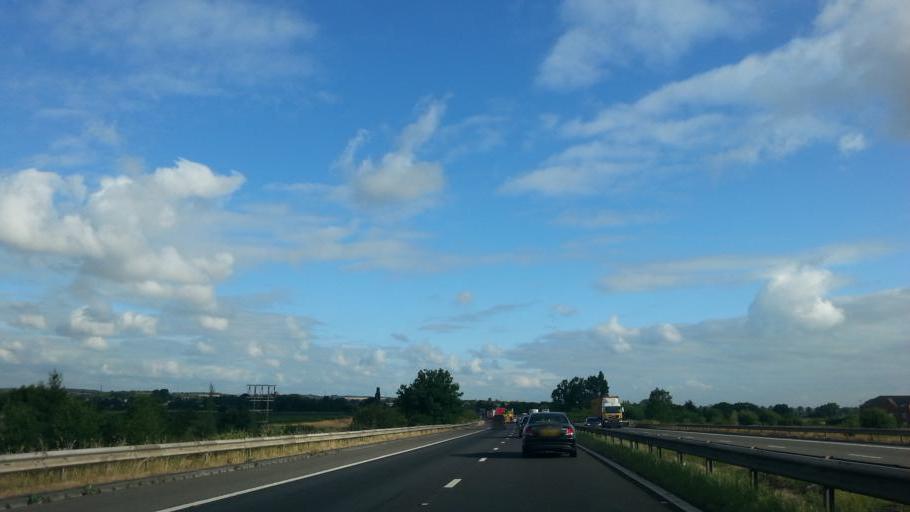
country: GB
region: England
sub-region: Doncaster
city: Tickhill
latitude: 53.4167
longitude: -1.0861
